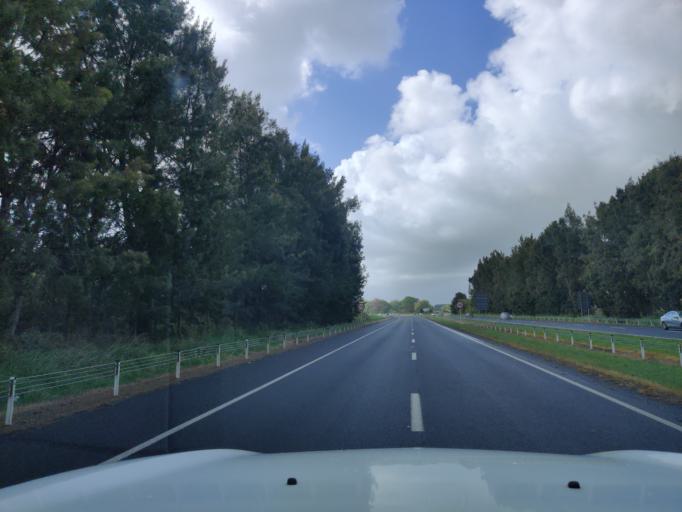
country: NZ
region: Waikato
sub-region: Waipa District
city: Cambridge
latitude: -37.8370
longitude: 175.3663
